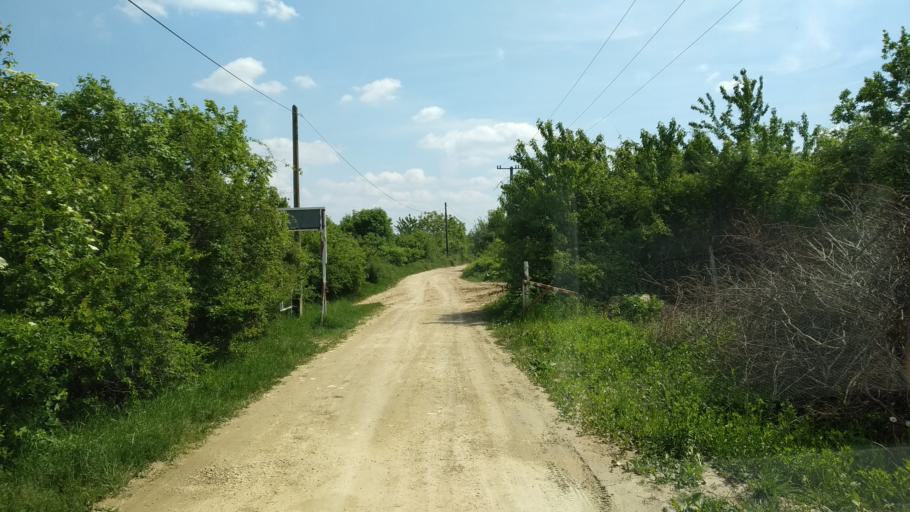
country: HU
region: Pest
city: Pomaz
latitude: 47.6198
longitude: 19.0231
